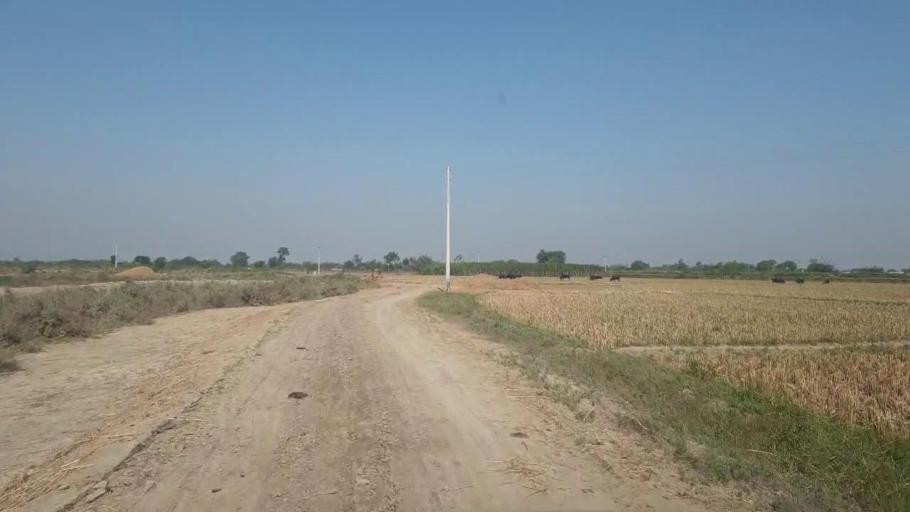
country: PK
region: Sindh
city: Badin
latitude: 24.6934
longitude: 68.8780
